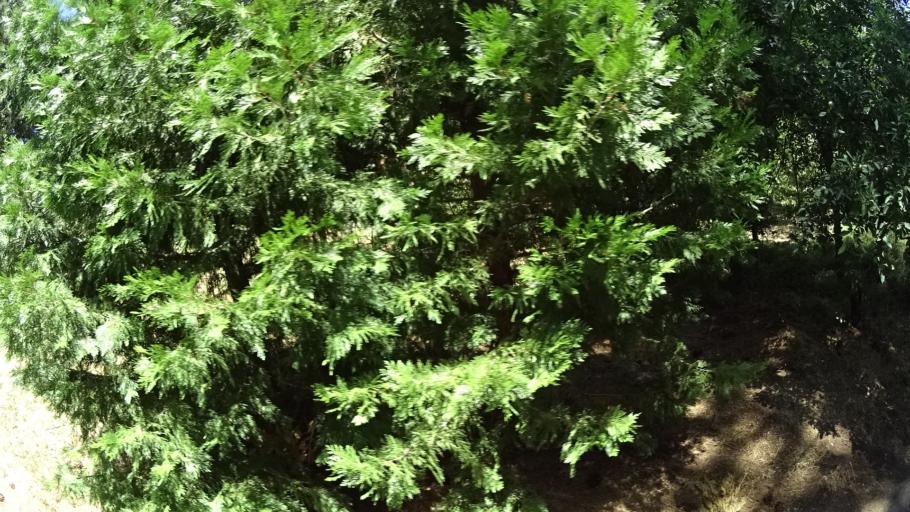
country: US
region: California
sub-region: Calaveras County
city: Forest Meadows
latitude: 38.1936
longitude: -120.3681
